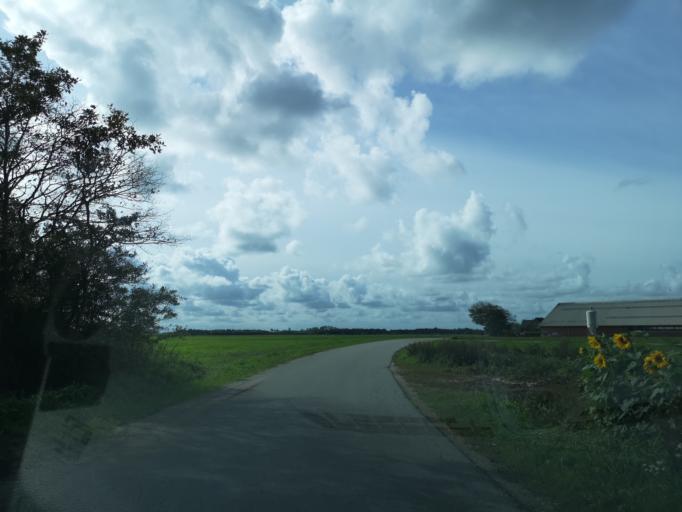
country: DK
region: Central Jutland
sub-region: Ringkobing-Skjern Kommune
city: Tarm
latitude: 55.9519
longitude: 8.5499
